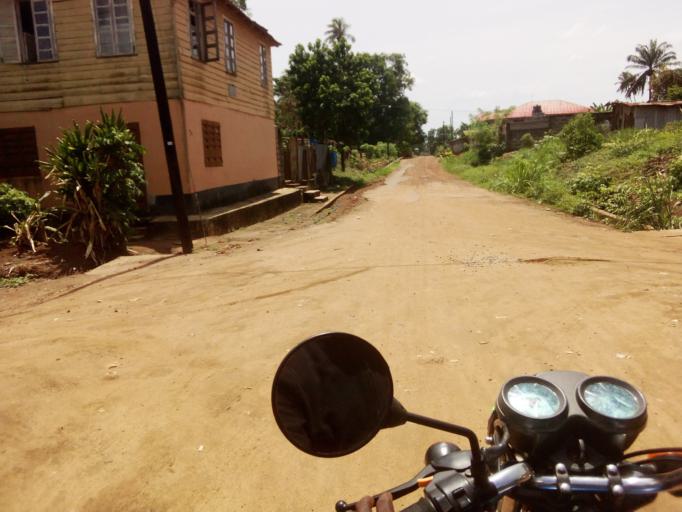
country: SL
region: Western Area
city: Waterloo
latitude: 8.3399
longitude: -13.0688
